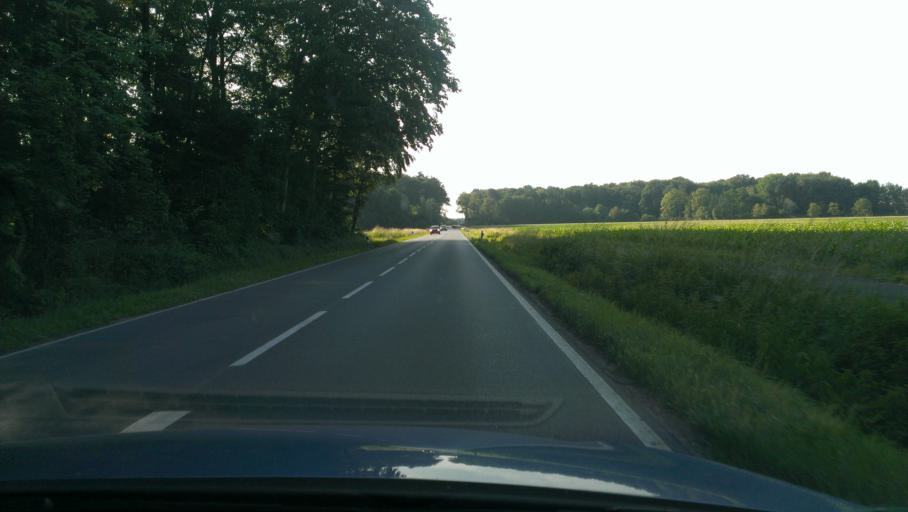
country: DE
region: North Rhine-Westphalia
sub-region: Regierungsbezirk Munster
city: Drensteinfurt
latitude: 51.8780
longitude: 7.7254
